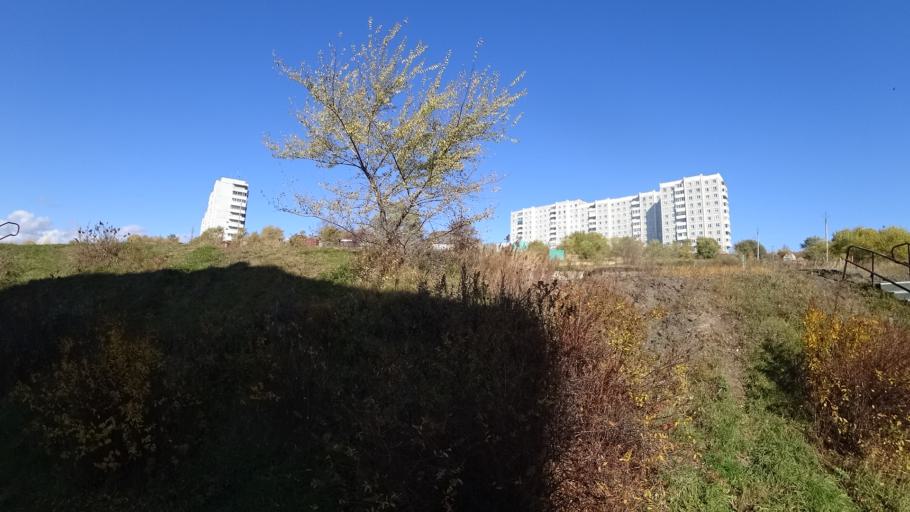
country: RU
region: Khabarovsk Krai
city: Amursk
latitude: 50.2387
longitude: 136.9170
